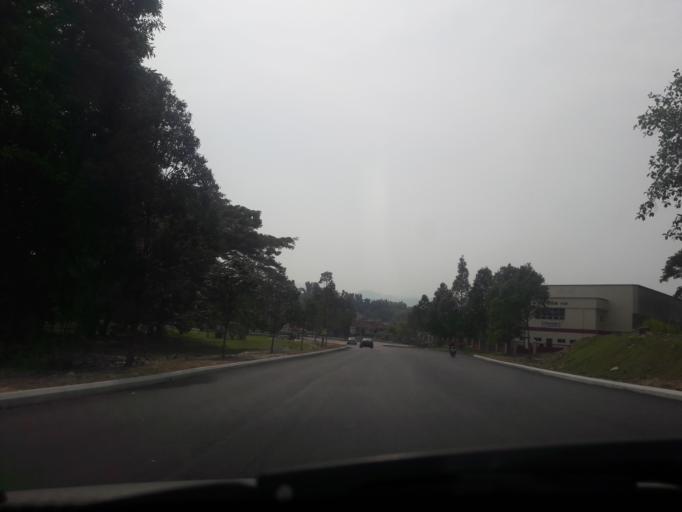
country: MY
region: Kedah
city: Kulim
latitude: 5.3682
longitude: 100.5598
